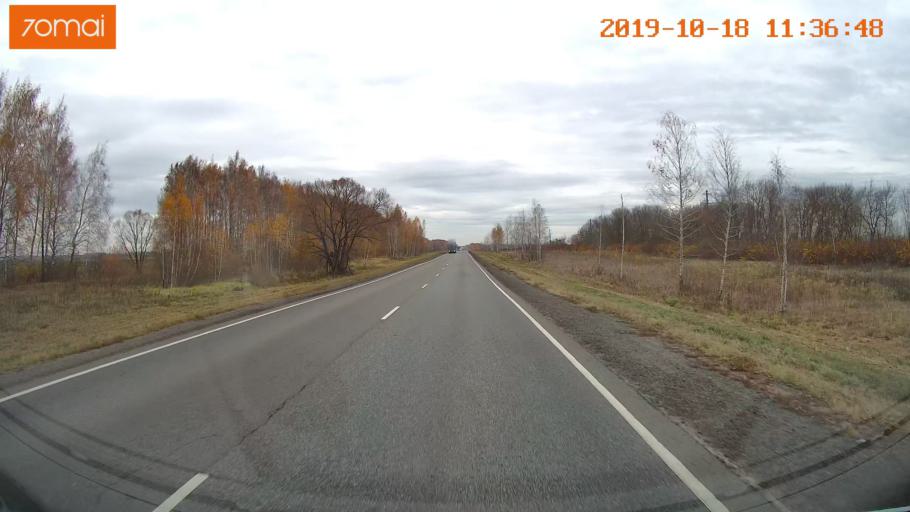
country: RU
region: Rjazan
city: Oktyabr'skiy
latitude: 54.1450
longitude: 38.8153
